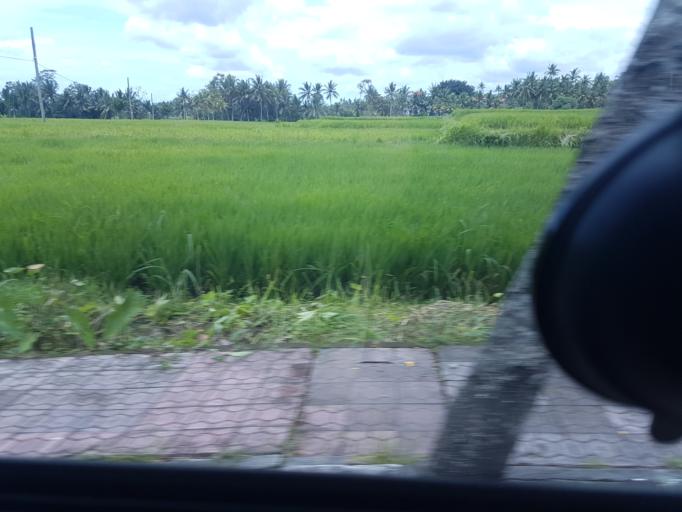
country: ID
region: Bali
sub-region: Kabupaten Gianyar
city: Ubud
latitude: -8.5188
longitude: 115.2933
